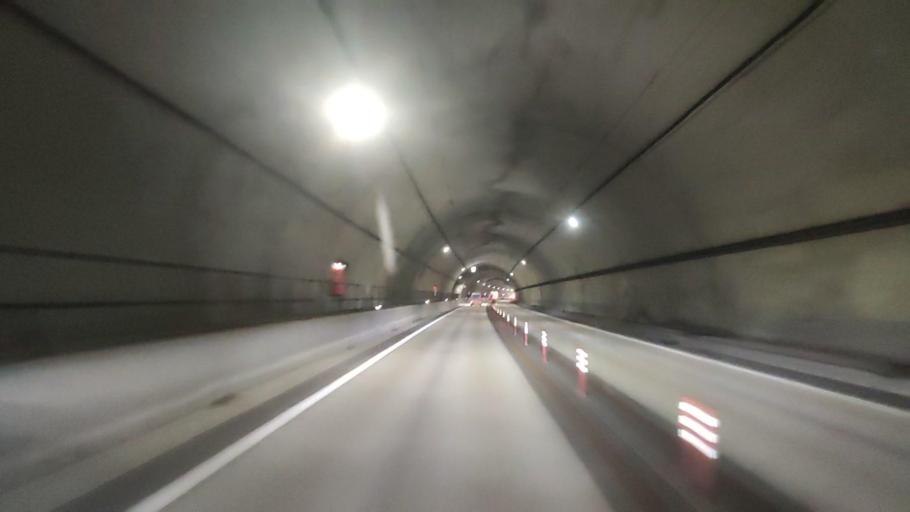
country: JP
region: Wakayama
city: Tanabe
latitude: 33.5925
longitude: 135.4379
